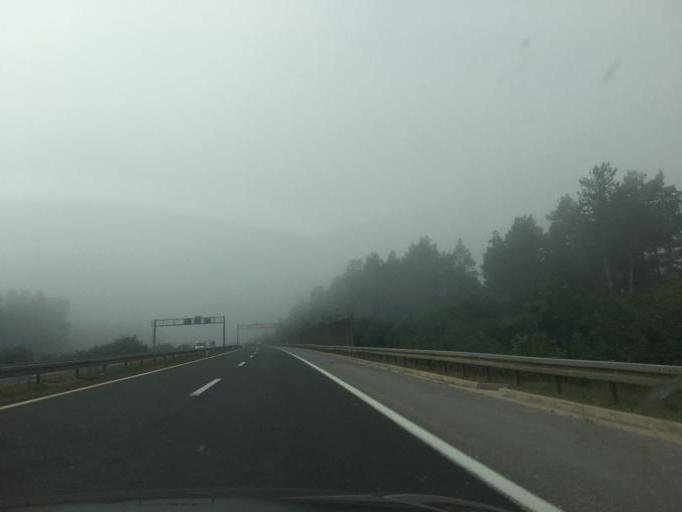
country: HR
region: Licko-Senjska
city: Gospic
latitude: 44.5849
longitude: 15.4314
